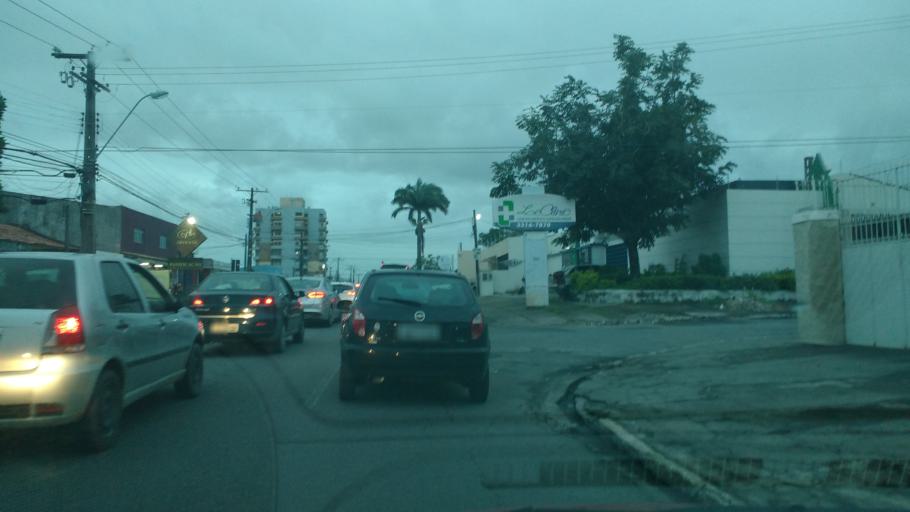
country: BR
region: Alagoas
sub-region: Maceio
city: Maceio
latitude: -9.6272
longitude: -35.7349
